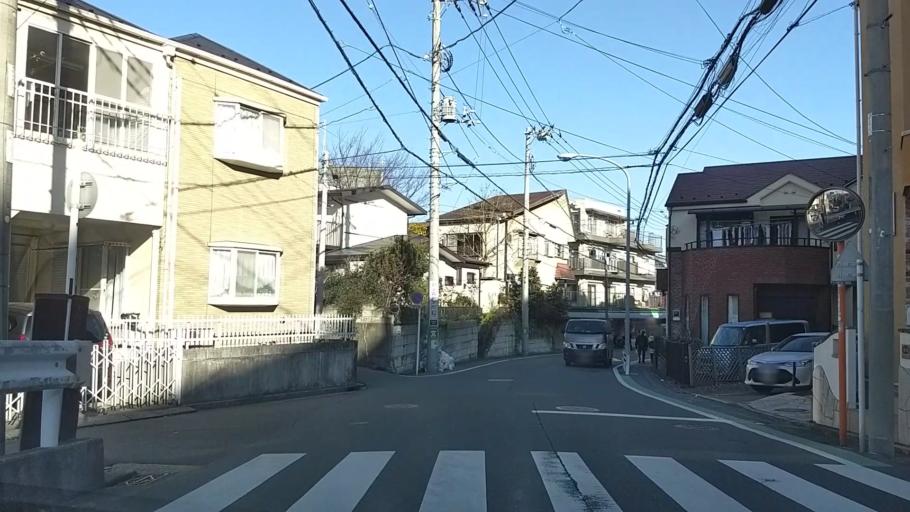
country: JP
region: Kanagawa
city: Yokohama
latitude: 35.4240
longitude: 139.6113
